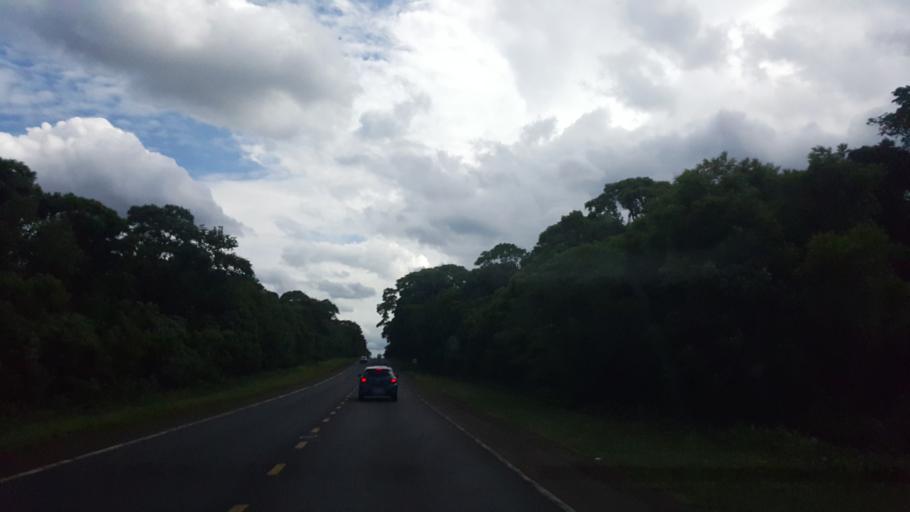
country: AR
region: Misiones
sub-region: Departamento de Iguazu
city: Puerto Iguazu
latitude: -25.7062
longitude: -54.5157
